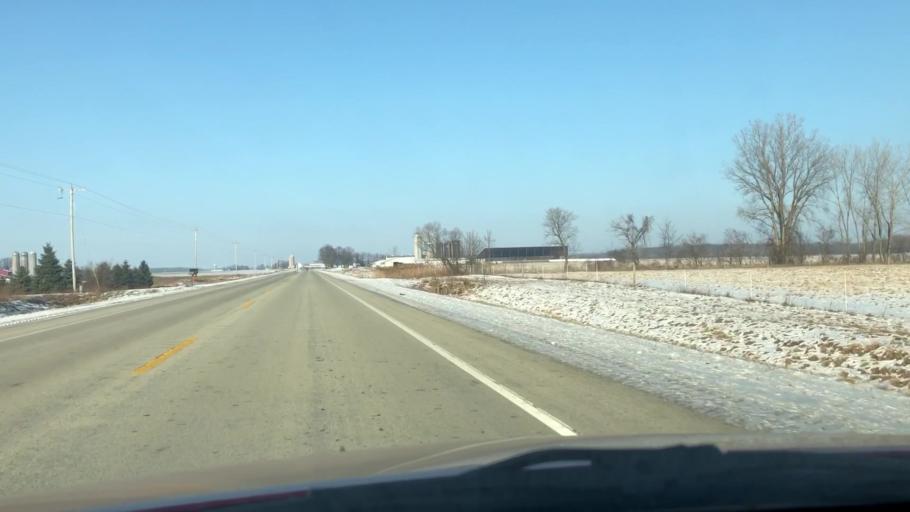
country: US
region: Wisconsin
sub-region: Outagamie County
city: Seymour
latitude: 44.4494
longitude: -88.3306
